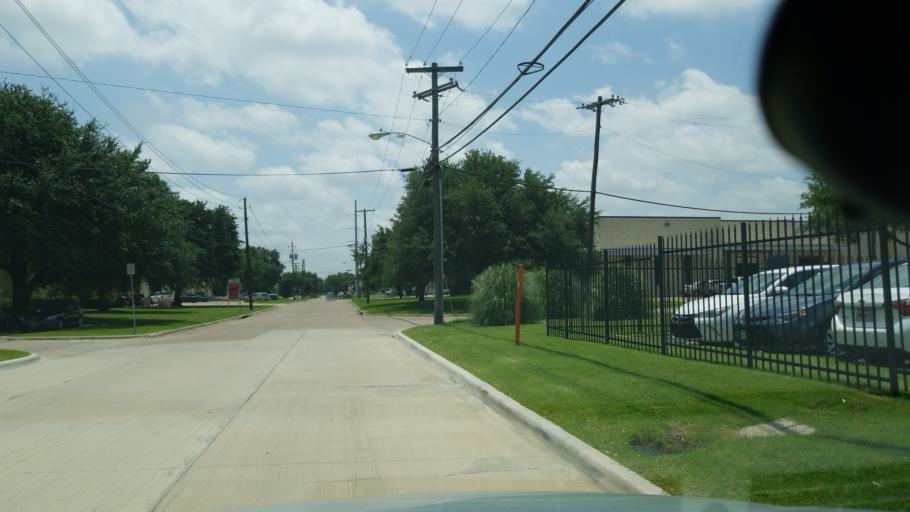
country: US
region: Texas
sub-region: Dallas County
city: Irving
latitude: 32.8276
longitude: -96.8755
